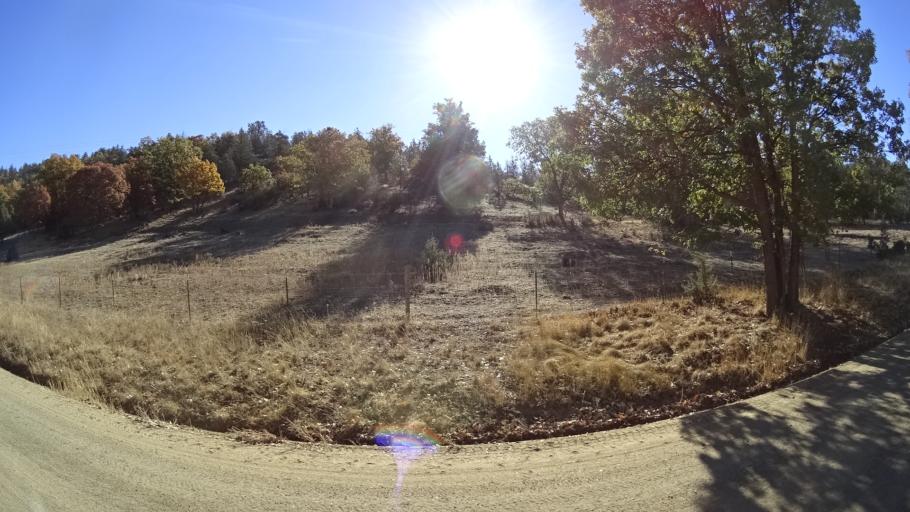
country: US
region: California
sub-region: Siskiyou County
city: Yreka
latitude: 41.5783
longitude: -122.7883
